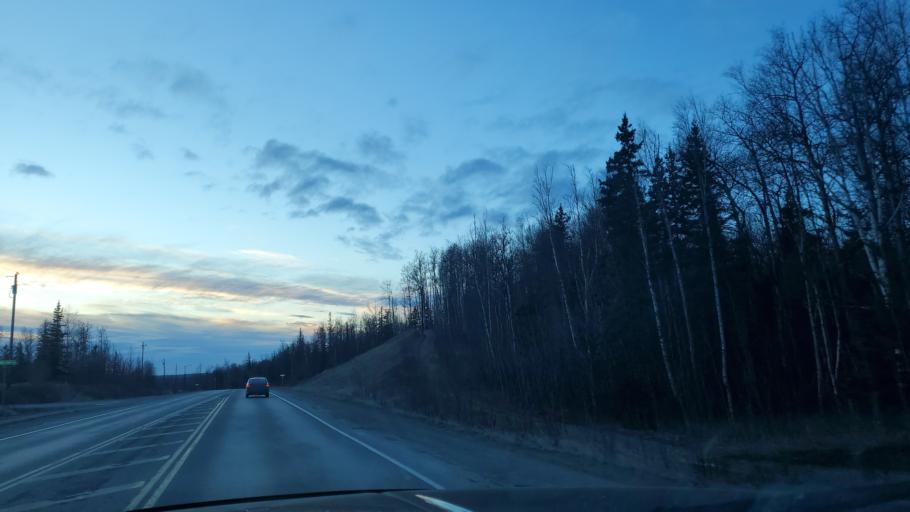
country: US
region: Alaska
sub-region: Matanuska-Susitna Borough
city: Wasilla
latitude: 61.5978
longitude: -149.4251
